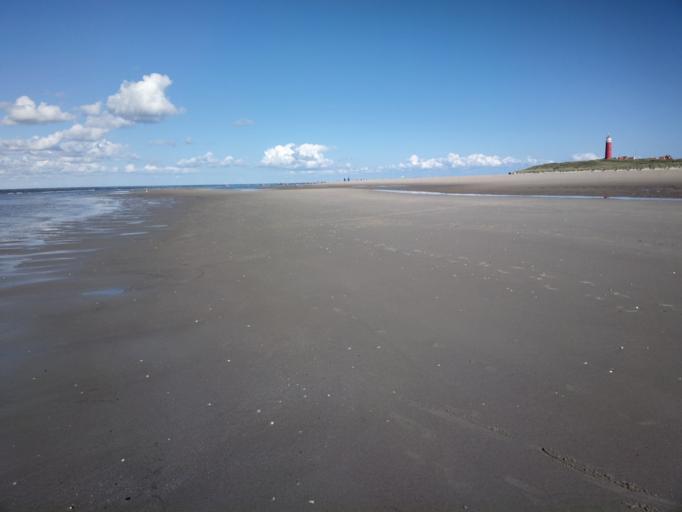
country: NL
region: North Holland
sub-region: Gemeente Texel
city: Den Burg
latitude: 53.1847
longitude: 4.8458
